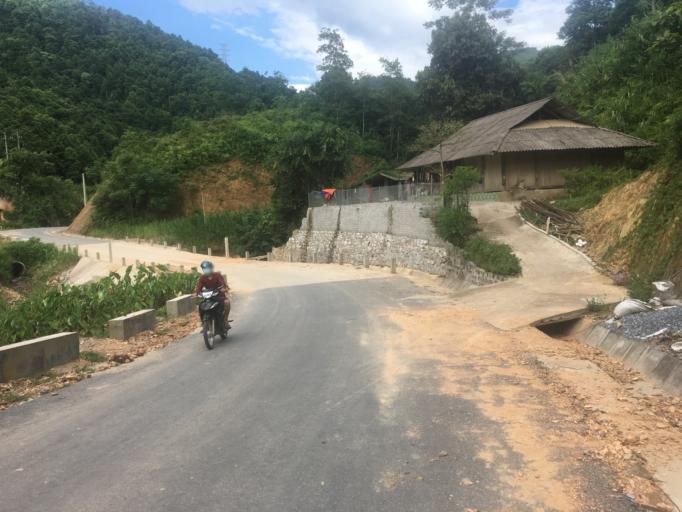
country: VN
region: Ha Giang
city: Thanh Pho Ha Giang
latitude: 22.8558
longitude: 105.0409
